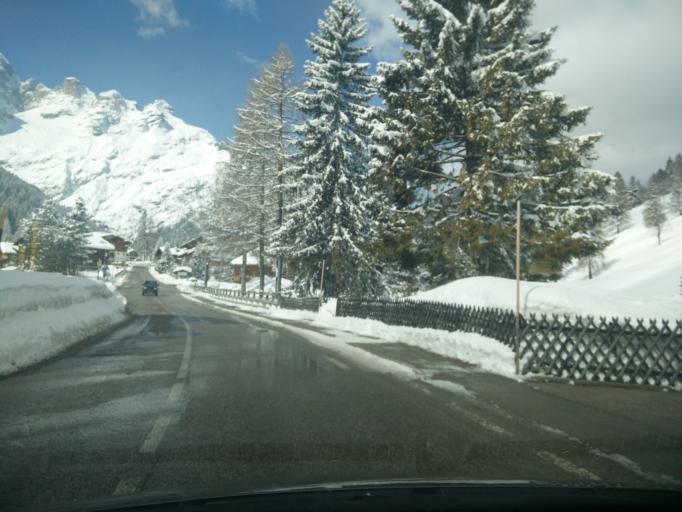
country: IT
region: Veneto
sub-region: Provincia di Belluno
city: Fusine
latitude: 46.3914
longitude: 12.1093
